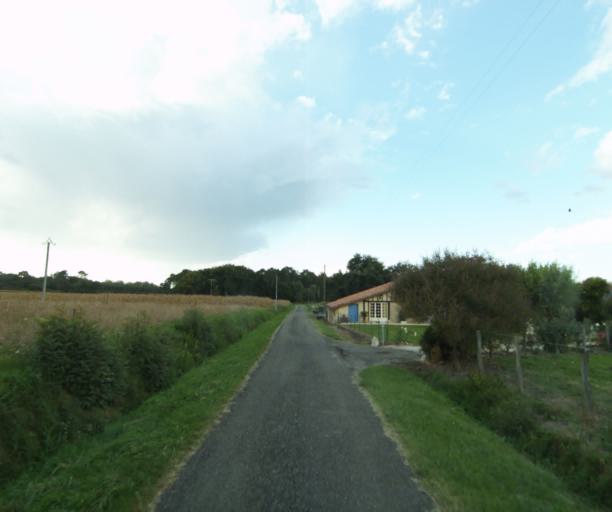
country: FR
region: Midi-Pyrenees
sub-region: Departement du Gers
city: Cazaubon
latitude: 43.9254
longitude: -0.0845
